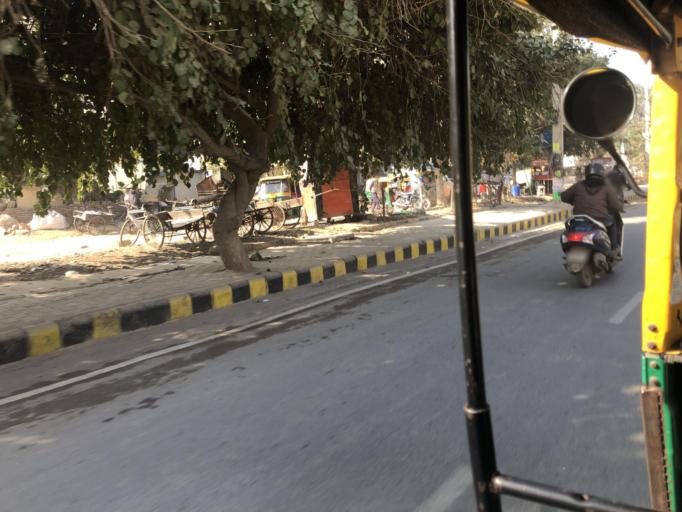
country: IN
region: Haryana
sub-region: Gurgaon
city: Gurgaon
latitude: 28.4488
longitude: 77.0725
